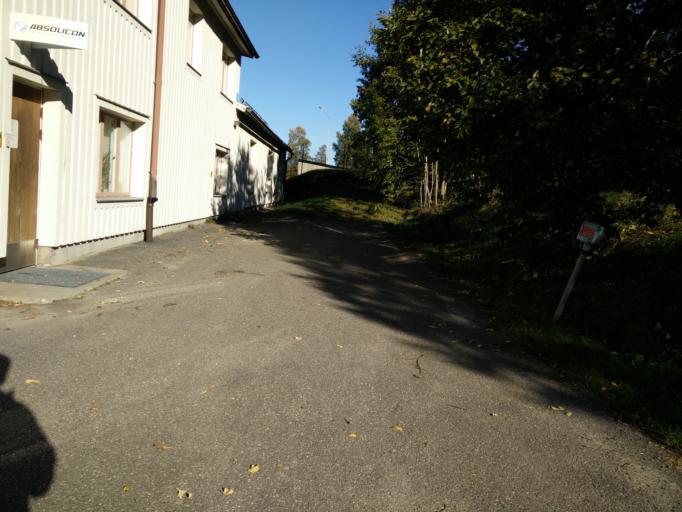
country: SE
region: Vaesternorrland
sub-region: Haernoesands Kommun
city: Haernoesand
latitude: 62.6399
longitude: 17.9510
